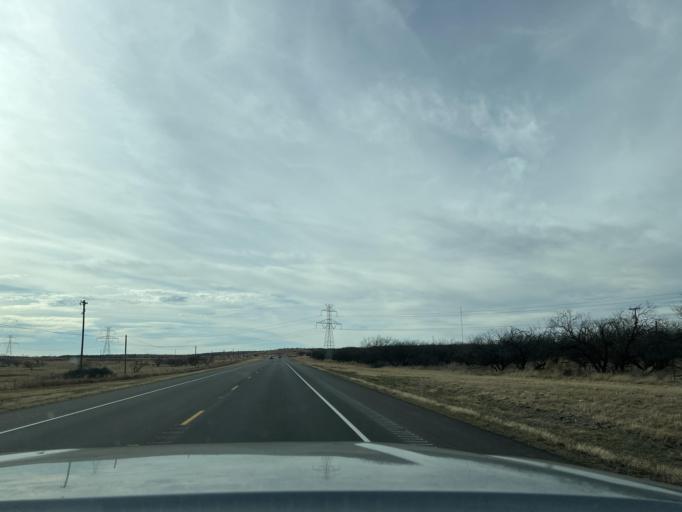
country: US
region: Texas
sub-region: Shackelford County
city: Albany
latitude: 32.7054
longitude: -99.4003
